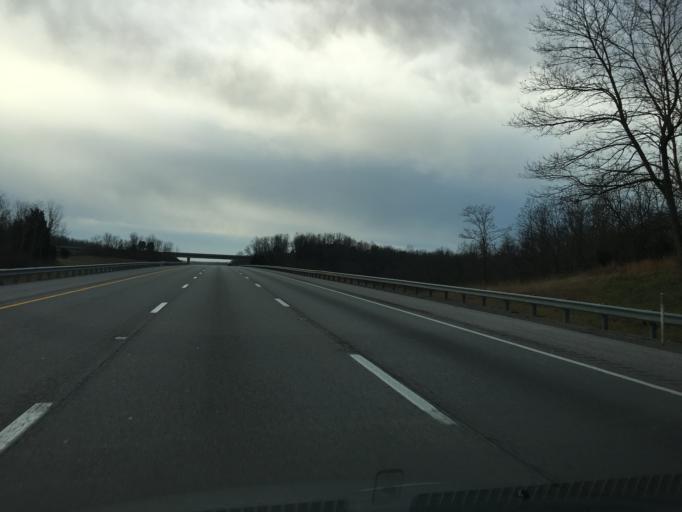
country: US
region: Kentucky
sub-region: Grant County
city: Williamstown
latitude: 38.4361
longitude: -84.5715
